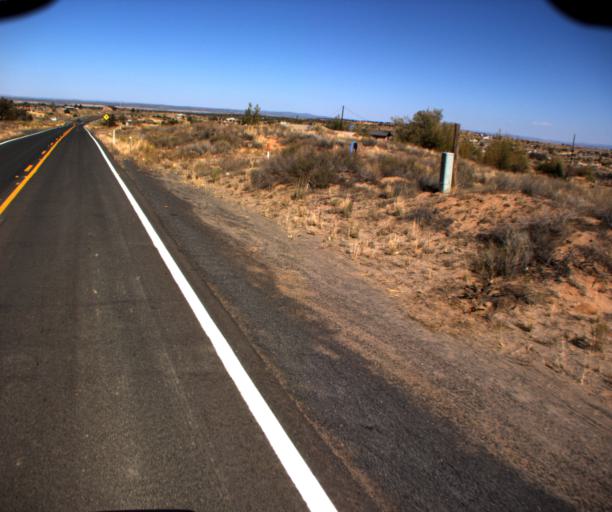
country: US
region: Arizona
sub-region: Navajo County
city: First Mesa
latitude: 35.9178
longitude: -110.6637
